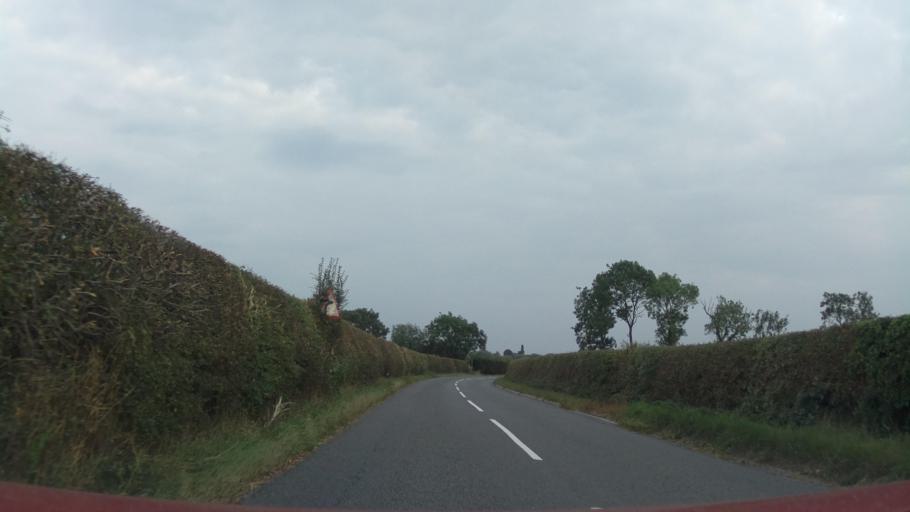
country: GB
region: England
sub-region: Lincolnshire
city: Skellingthorpe
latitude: 53.1386
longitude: -0.6454
